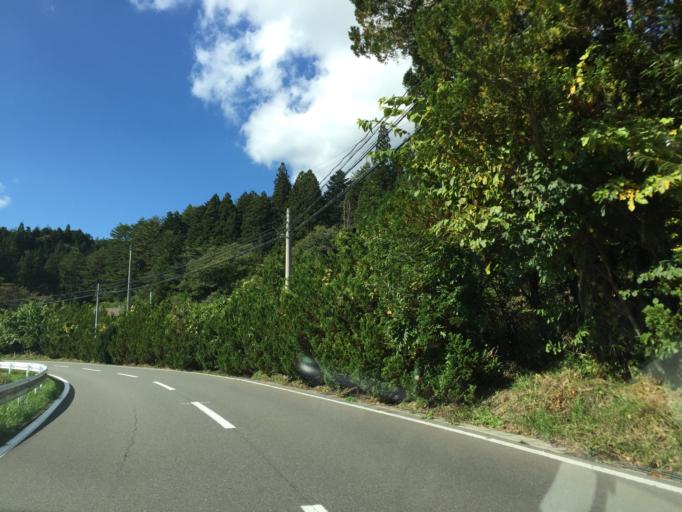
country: JP
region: Fukushima
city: Funehikimachi-funehiki
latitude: 37.5611
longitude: 140.7671
